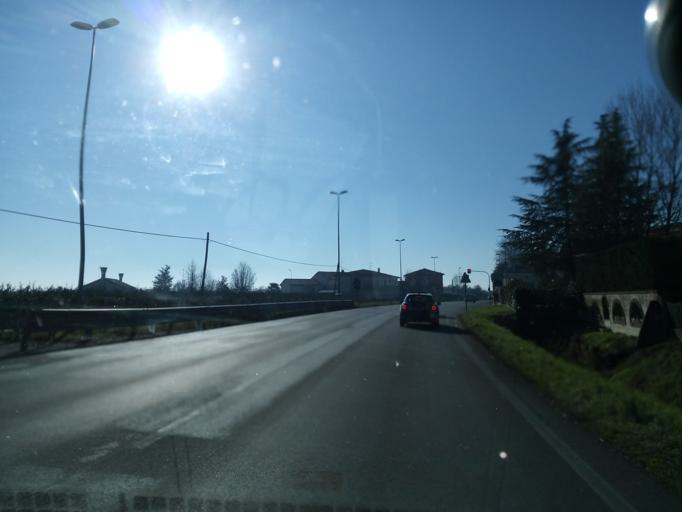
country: IT
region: Veneto
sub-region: Provincia di Venezia
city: Stigliano
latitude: 45.5256
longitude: 12.0491
